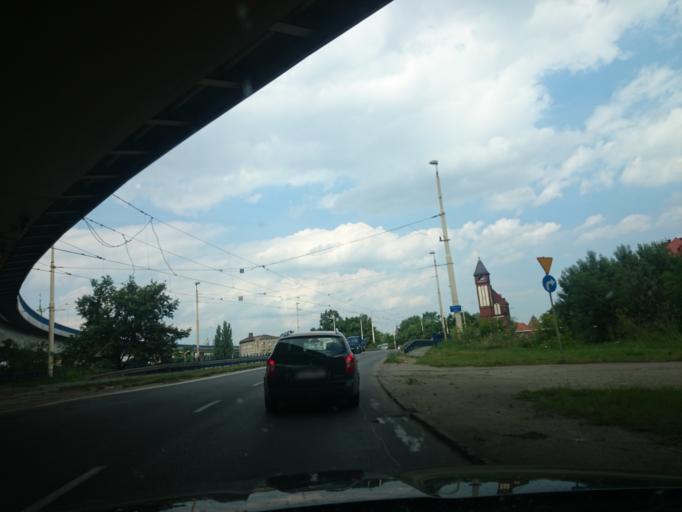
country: PL
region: West Pomeranian Voivodeship
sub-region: Szczecin
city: Szczecin
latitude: 53.4160
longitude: 14.5683
